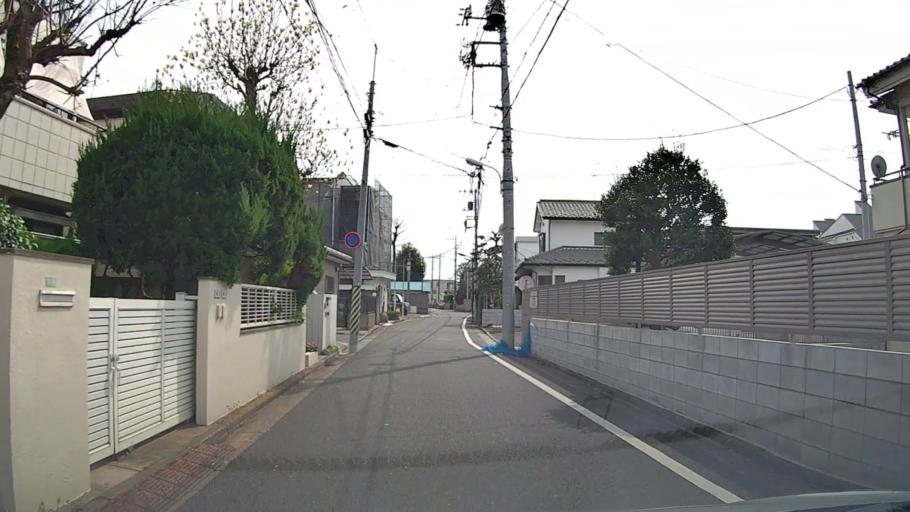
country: JP
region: Saitama
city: Wako
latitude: 35.7551
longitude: 139.6523
